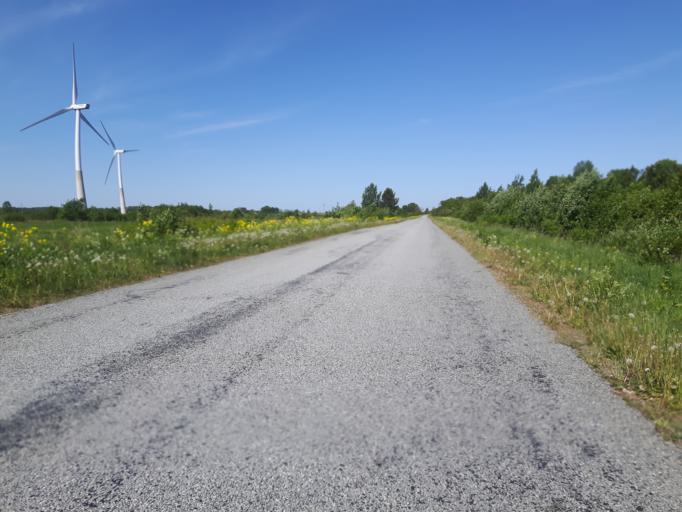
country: EE
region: Ida-Virumaa
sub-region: Aseri vald
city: Aseri
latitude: 59.4602
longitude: 26.8340
